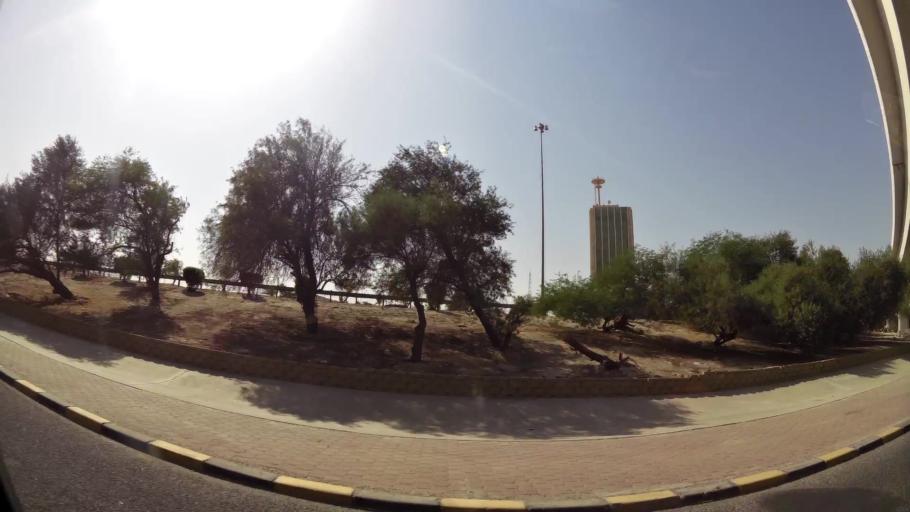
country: KW
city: Bayan
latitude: 29.3059
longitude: 48.0224
